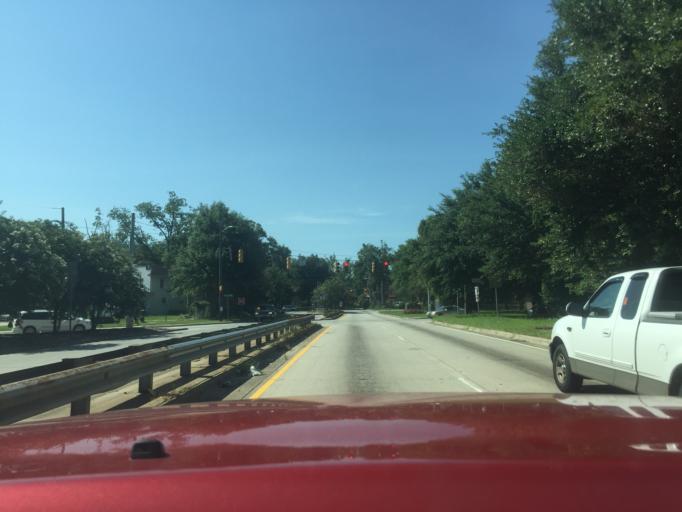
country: US
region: Georgia
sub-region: Chatham County
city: Savannah
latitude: 32.0615
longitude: -81.1110
